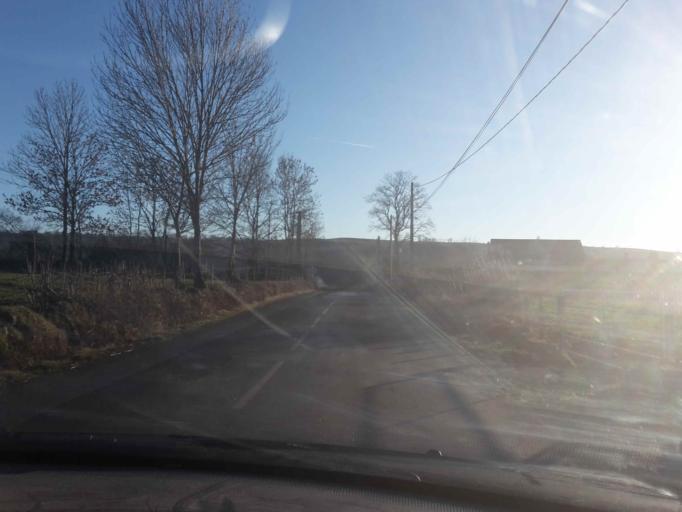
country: FR
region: Auvergne
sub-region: Departement du Cantal
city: Ydes
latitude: 45.2442
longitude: 2.5408
